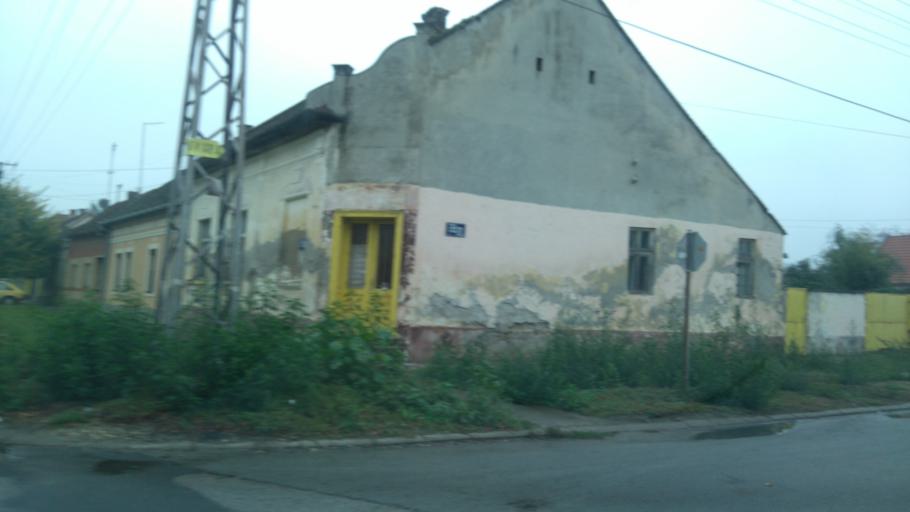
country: RS
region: Autonomna Pokrajina Vojvodina
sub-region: Juznobacki Okrug
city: Becej
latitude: 45.6140
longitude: 20.0401
